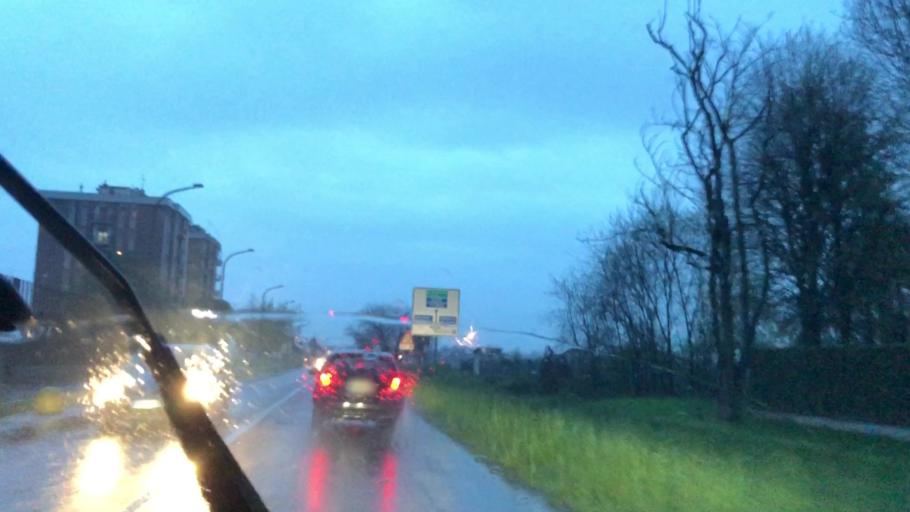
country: IT
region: Lombardy
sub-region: Citta metropolitana di Milano
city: Cusano Milanino
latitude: 45.5575
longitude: 9.1862
